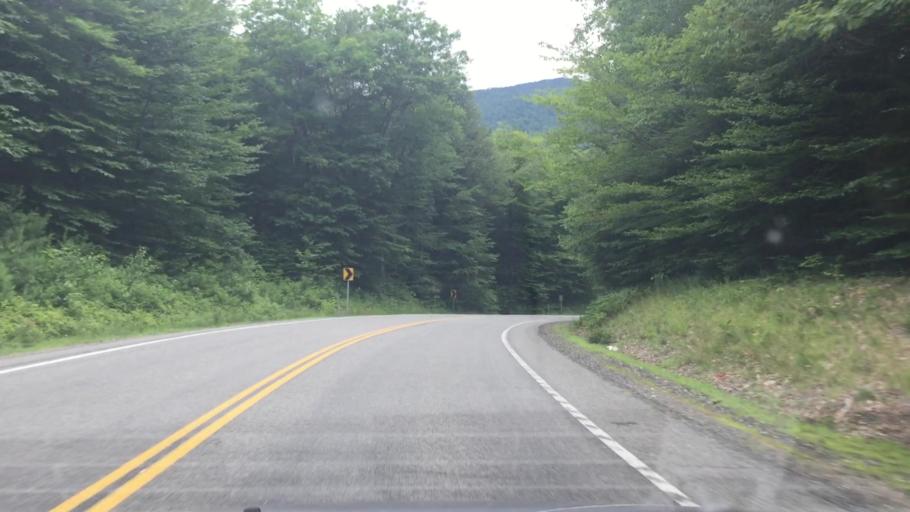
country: US
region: New Hampshire
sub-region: Carroll County
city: North Conway
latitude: 44.0792
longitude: -71.3444
